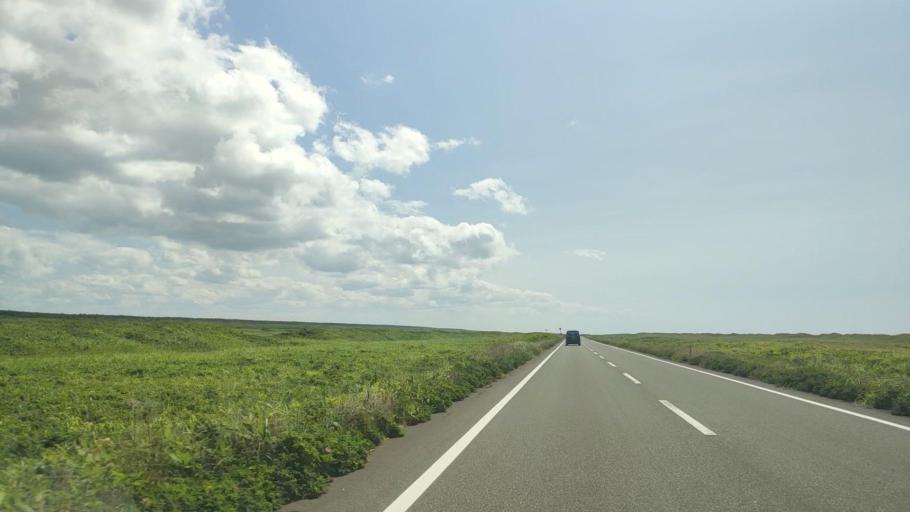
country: JP
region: Hokkaido
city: Wakkanai
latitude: 45.1602
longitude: 141.5863
